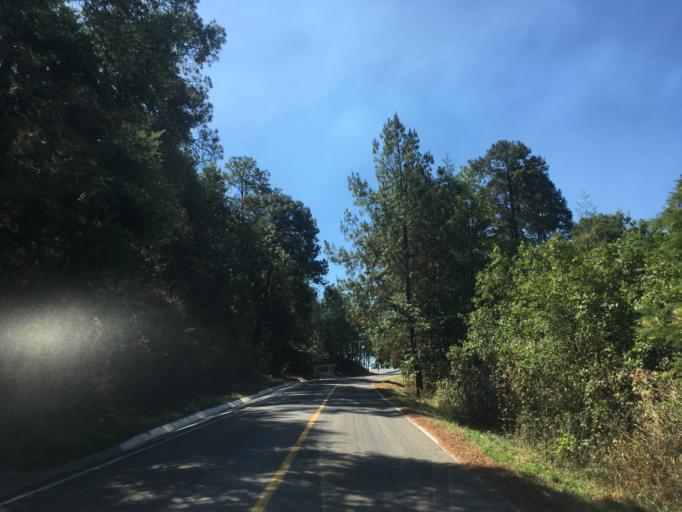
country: MX
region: Michoacan
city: Tzitzio
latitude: 19.6662
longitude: -100.9112
